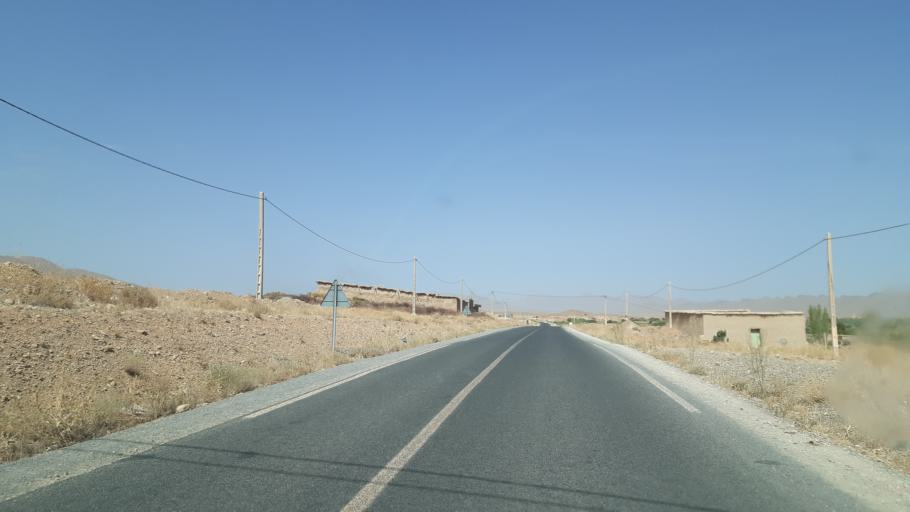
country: MA
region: Meknes-Tafilalet
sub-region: Errachidia
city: Amouguer
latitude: 32.2224
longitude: -4.6852
